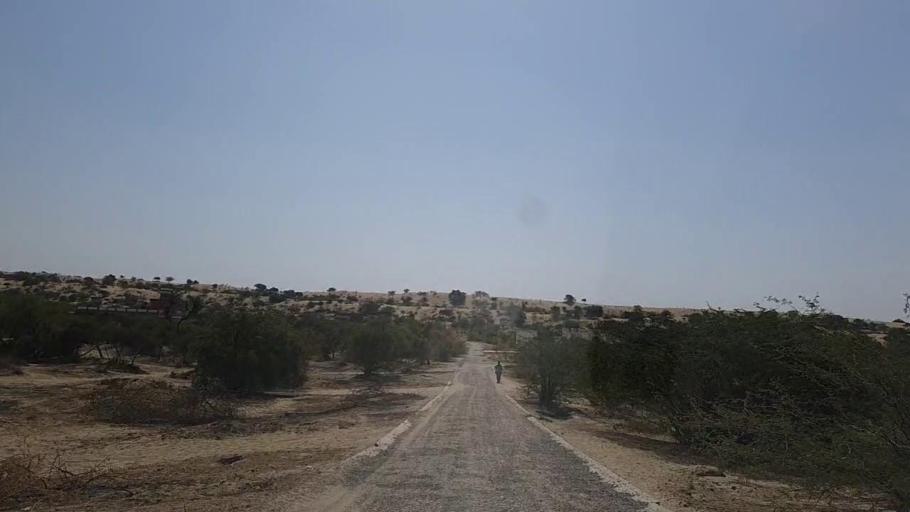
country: PK
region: Sindh
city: Mithi
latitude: 24.7048
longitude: 69.5918
